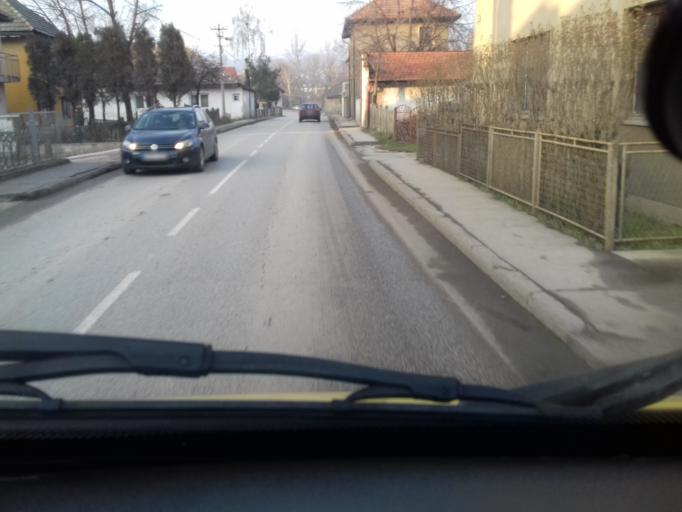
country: BA
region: Federation of Bosnia and Herzegovina
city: Kakanj
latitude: 44.1163
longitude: 18.1166
